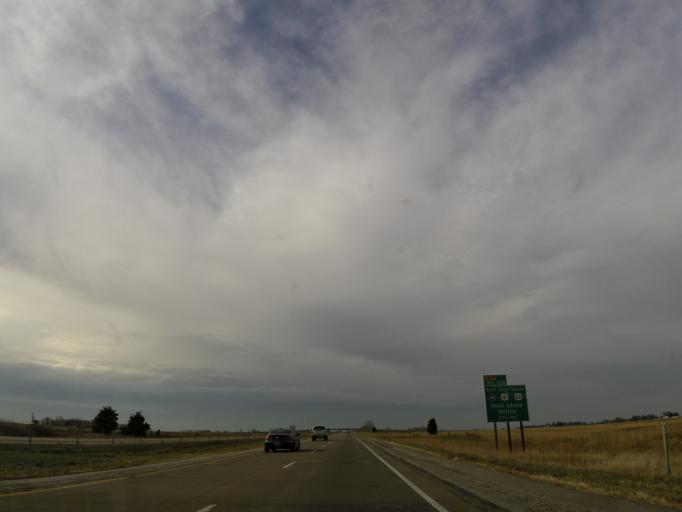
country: US
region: Iowa
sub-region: Scott County
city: Eldridge
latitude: 41.6007
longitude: -90.6358
